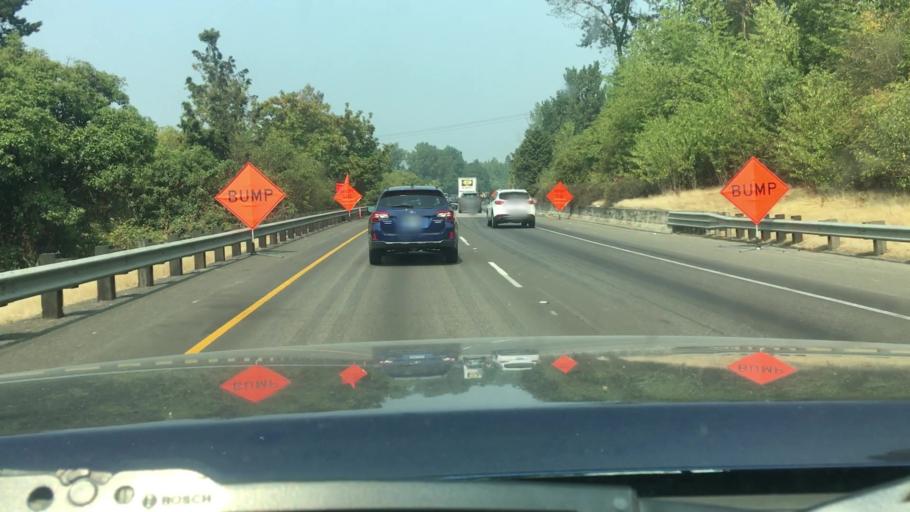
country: US
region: Oregon
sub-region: Clackamas County
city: West Linn
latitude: 45.3510
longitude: -122.6597
